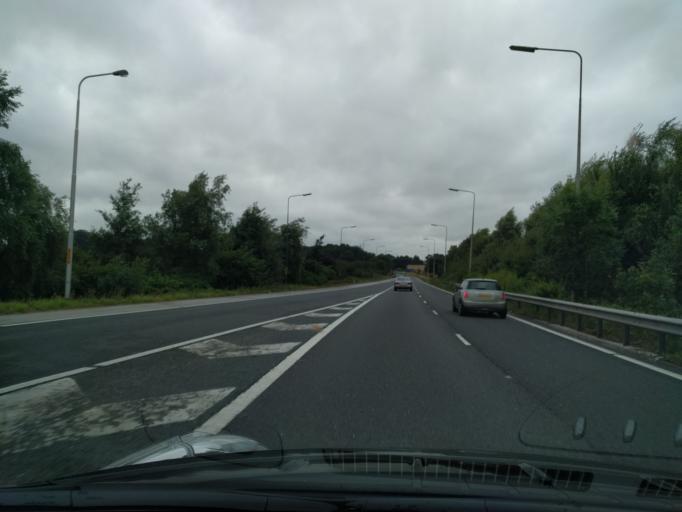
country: GB
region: England
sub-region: Warrington
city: Croft
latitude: 53.4294
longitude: -2.5650
